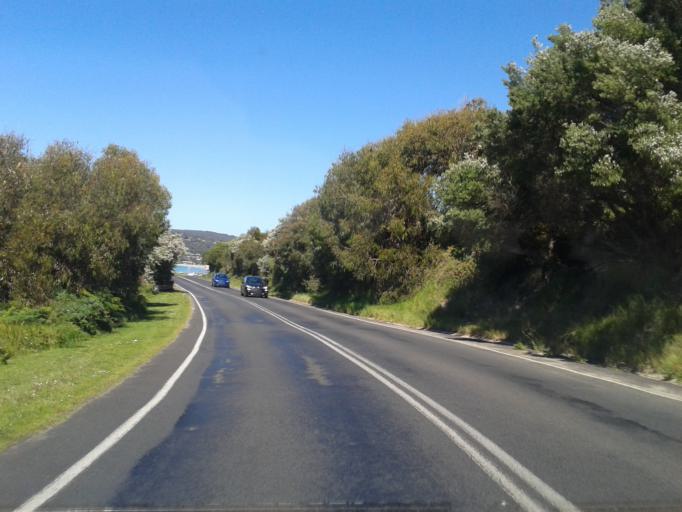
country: AU
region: Victoria
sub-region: Surf Coast
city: Anglesea
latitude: -38.5243
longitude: 143.9855
